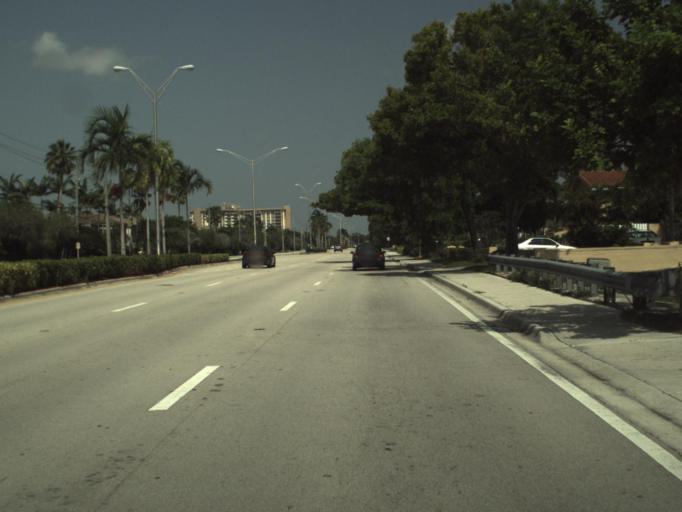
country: US
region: Florida
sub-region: Broward County
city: Coral Springs
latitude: 26.2726
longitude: -80.2778
